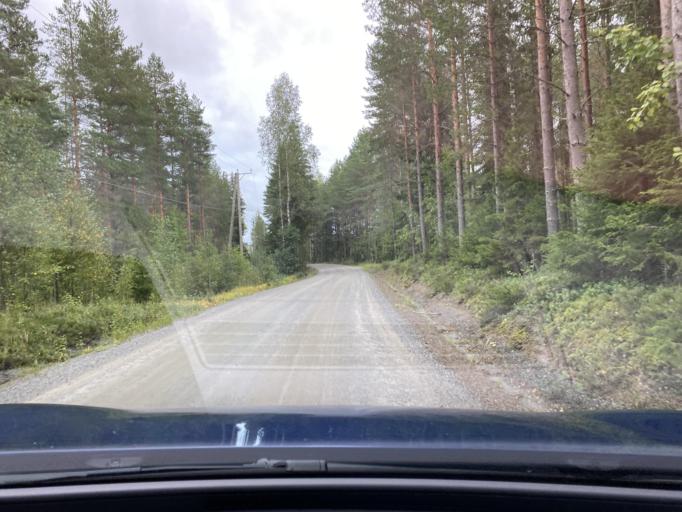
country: FI
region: Pirkanmaa
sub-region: Lounais-Pirkanmaa
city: Punkalaidun
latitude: 61.2306
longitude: 23.0972
